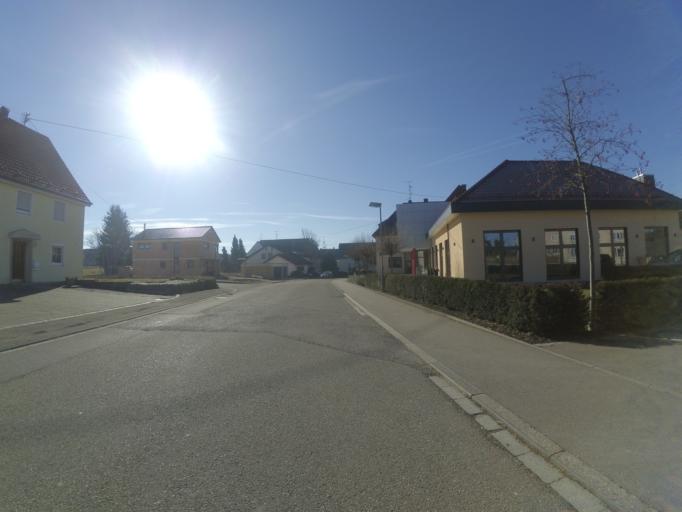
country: DE
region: Baden-Wuerttemberg
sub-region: Tuebingen Region
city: Erbach
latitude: 48.3007
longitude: 9.9071
